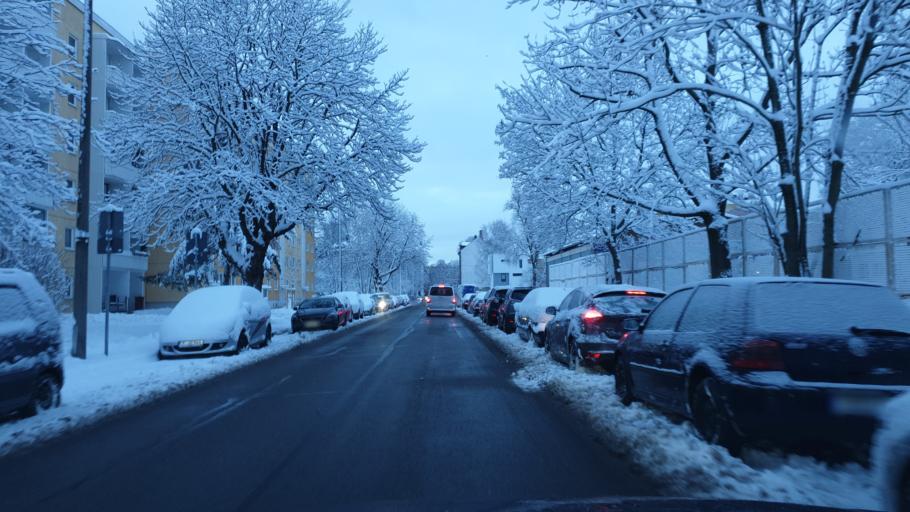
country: DE
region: Saxony
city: Chemnitz
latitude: 50.8438
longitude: 12.9193
